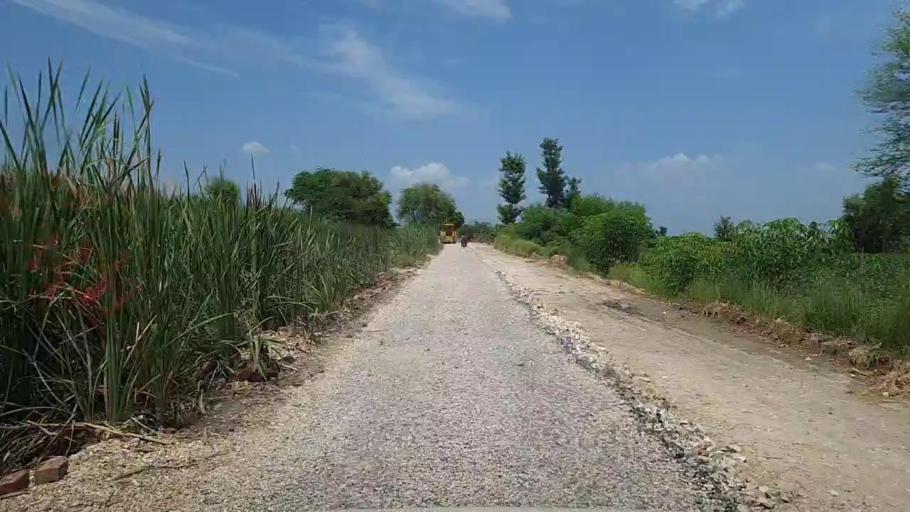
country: PK
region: Sindh
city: Bhiria
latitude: 26.9121
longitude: 68.2041
